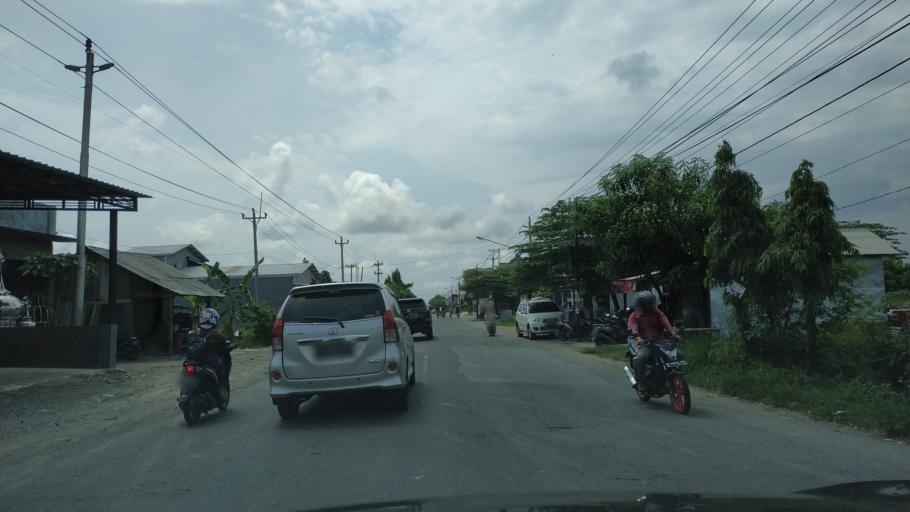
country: ID
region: Central Java
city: Adiwerna
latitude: -6.9246
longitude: 109.1259
